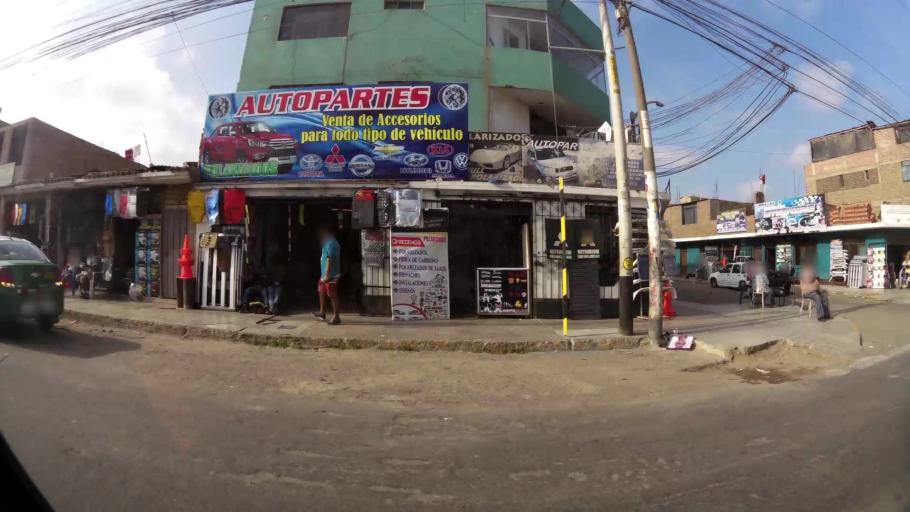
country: PE
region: La Libertad
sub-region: Provincia de Trujillo
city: El Porvenir
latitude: -8.0935
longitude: -79.0161
